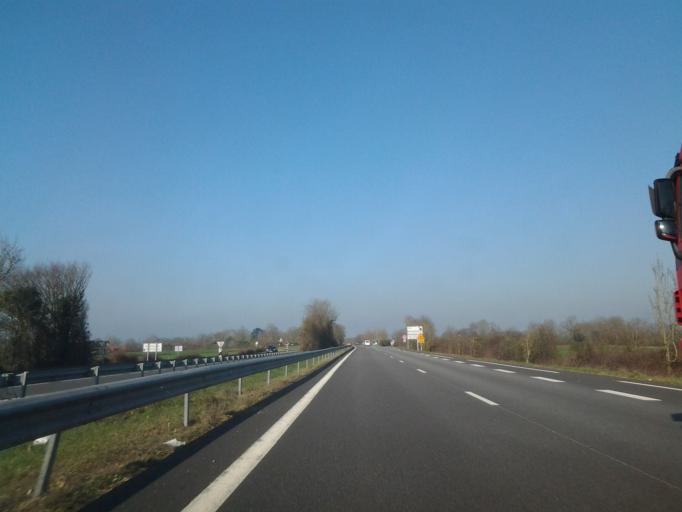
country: FR
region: Pays de la Loire
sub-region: Departement de la Vendee
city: Mouilleron-le-Captif
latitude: 46.6902
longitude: -1.4659
